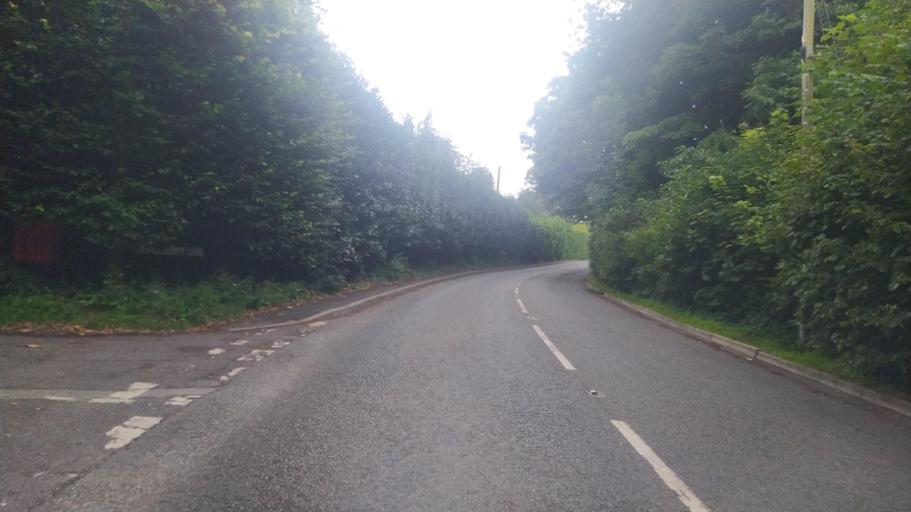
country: GB
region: England
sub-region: Hampshire
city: Liss
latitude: 51.0335
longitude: -0.8771
